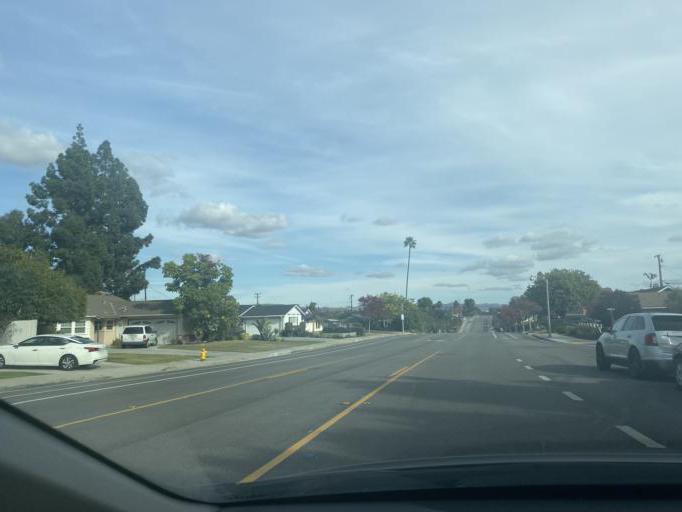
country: US
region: California
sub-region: Orange County
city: Brea
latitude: 33.9033
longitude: -117.9008
